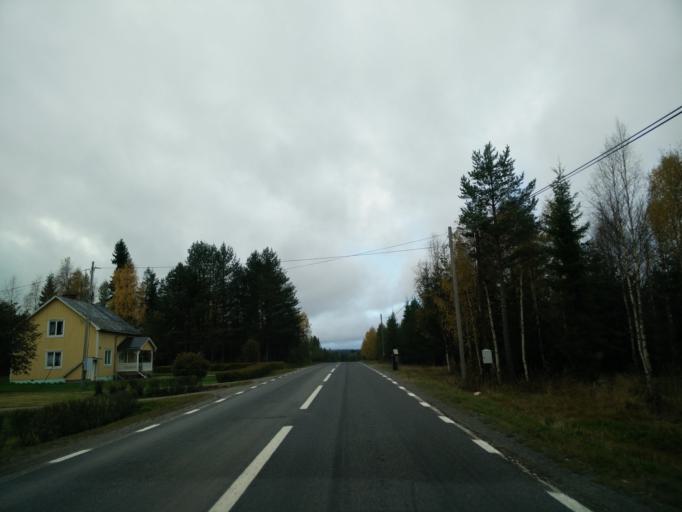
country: SE
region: Jaemtland
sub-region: Braecke Kommun
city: Braecke
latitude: 62.3992
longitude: 15.2428
